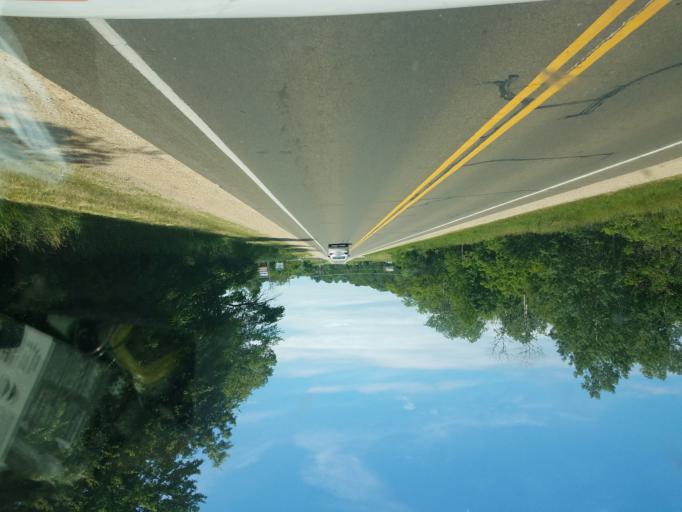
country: US
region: Wisconsin
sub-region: Sauk County
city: Reedsburg
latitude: 43.5764
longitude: -90.1091
